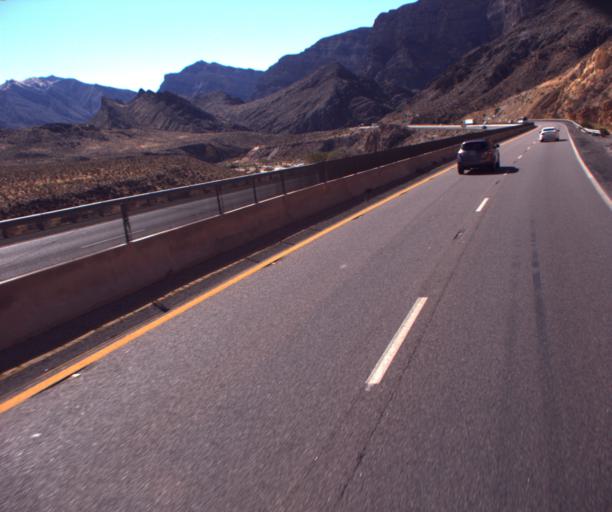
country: US
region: Arizona
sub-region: Mohave County
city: Beaver Dam
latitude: 36.9468
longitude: -113.8069
